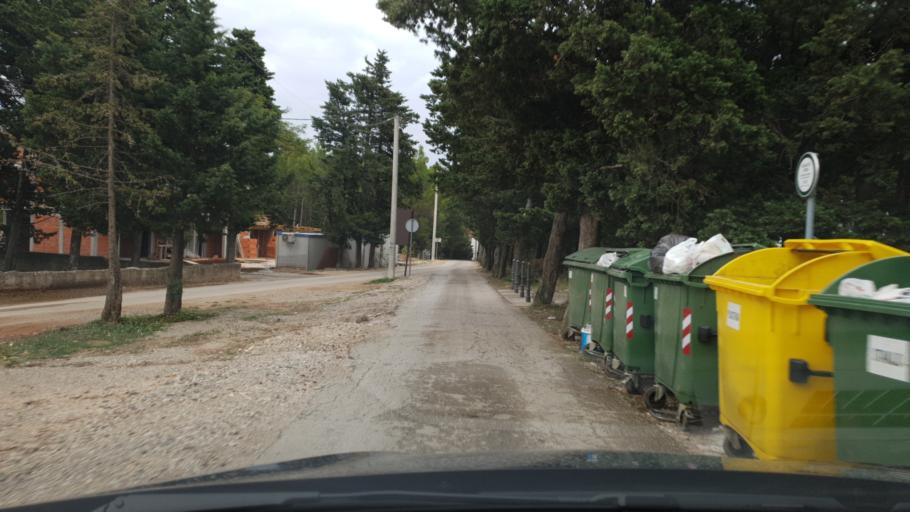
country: HR
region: Dubrovacko-Neretvanska
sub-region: Grad Dubrovnik
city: Dubrovnik
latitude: 42.6434
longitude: 18.1264
